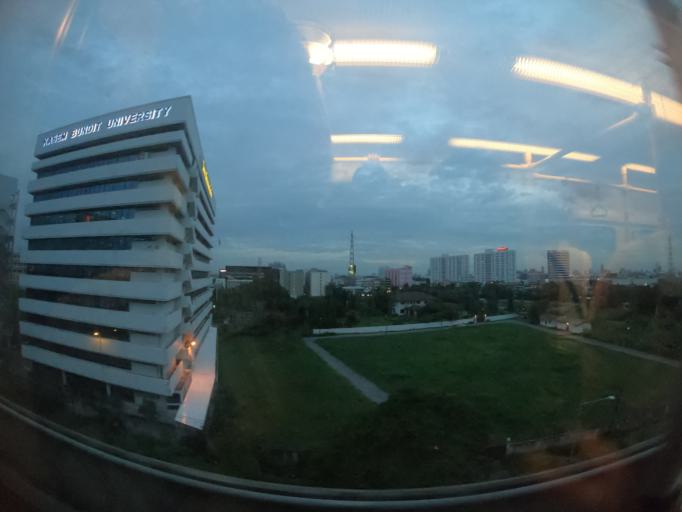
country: TH
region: Bangkok
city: Suan Luang
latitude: 13.7400
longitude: 100.6259
